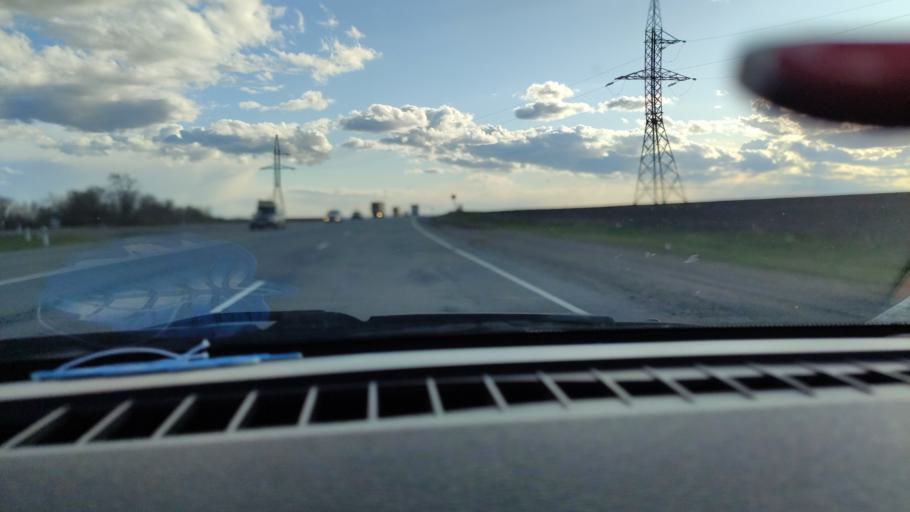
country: RU
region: Saratov
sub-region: Saratovskiy Rayon
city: Saratov
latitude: 51.7446
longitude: 46.0507
